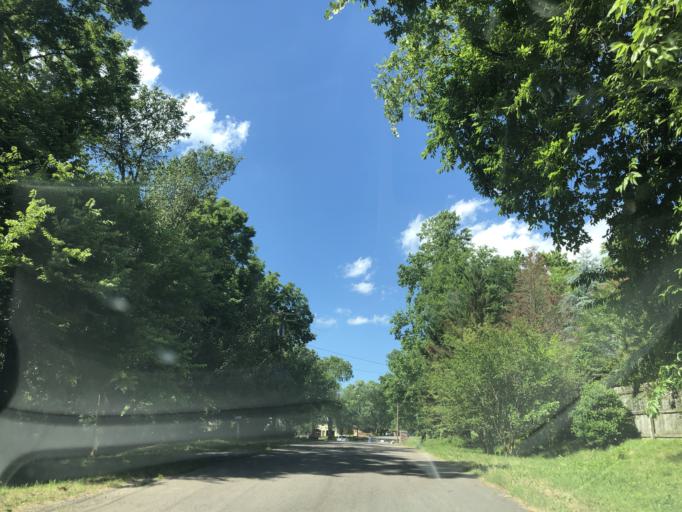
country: US
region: Tennessee
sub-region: Davidson County
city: Belle Meade
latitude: 36.0649
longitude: -86.9297
